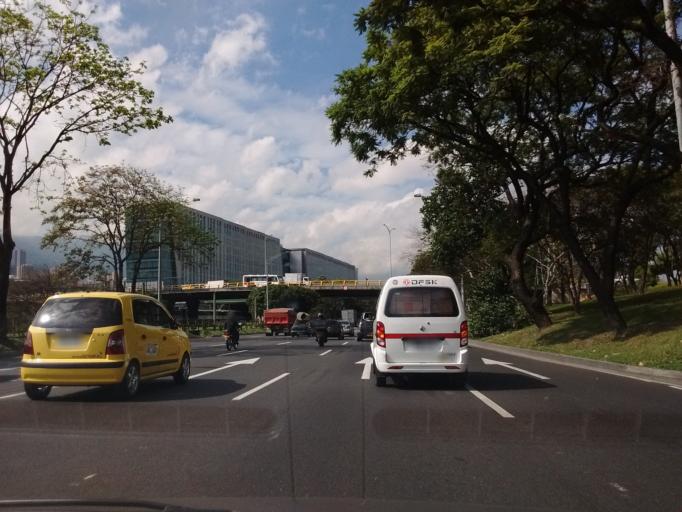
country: CO
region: Antioquia
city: Medellin
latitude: 6.2326
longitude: -75.5760
